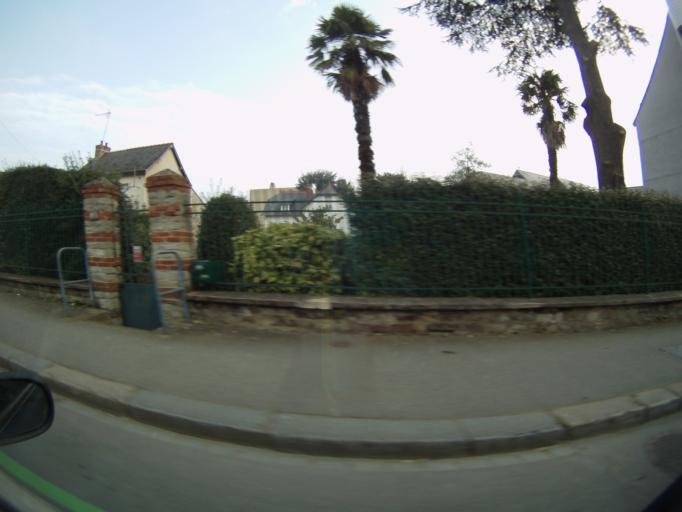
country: FR
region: Brittany
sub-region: Departement d'Ille-et-Vilaine
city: Rennes
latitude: 48.0986
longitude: -1.6564
